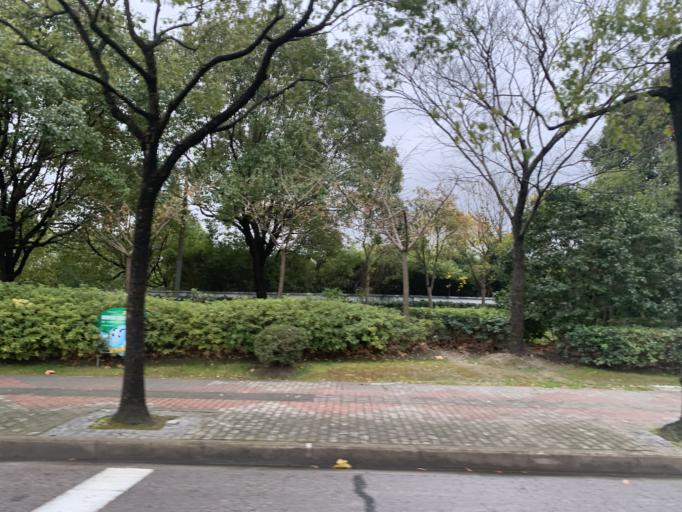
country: CN
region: Shanghai Shi
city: Huamu
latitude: 31.1954
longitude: 121.5394
